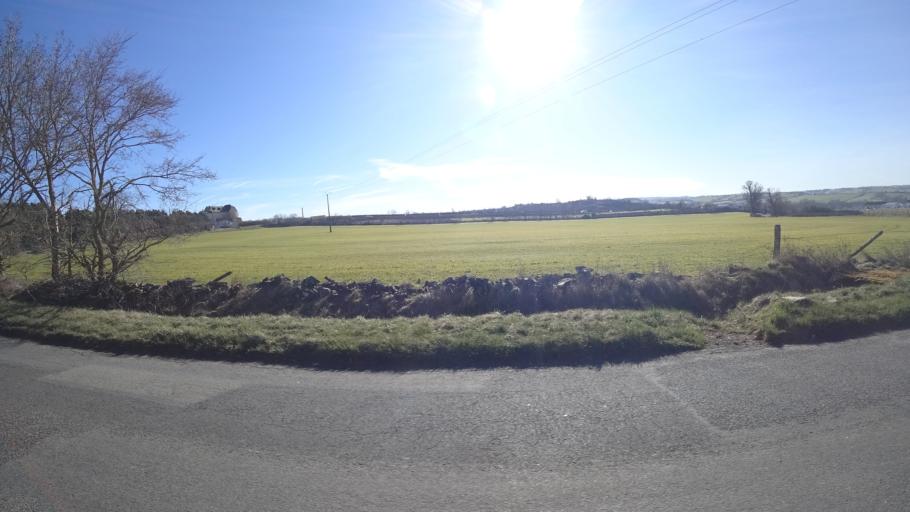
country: FR
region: Midi-Pyrenees
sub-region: Departement de l'Aveyron
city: Sebazac-Concoures
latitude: 44.3875
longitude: 2.5904
